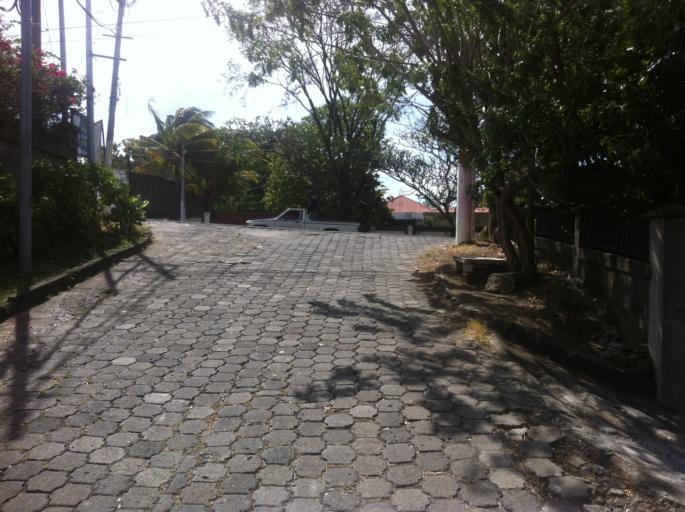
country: NI
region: Managua
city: El Crucero
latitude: 12.0706
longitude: -86.3216
